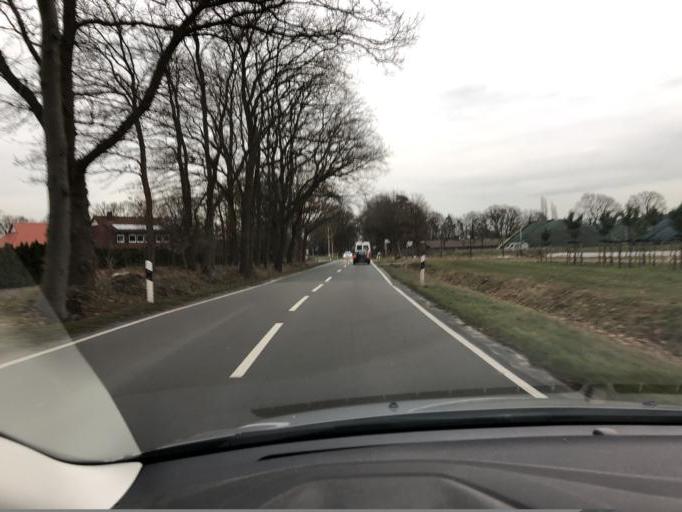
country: DE
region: Lower Saxony
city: Wiefelstede
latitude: 53.1939
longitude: 8.1248
